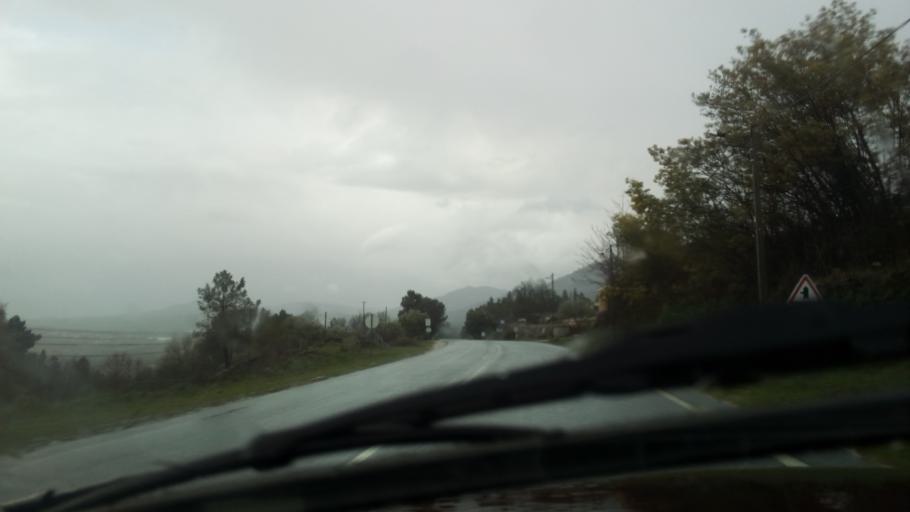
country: PT
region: Guarda
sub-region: Guarda
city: Guarda
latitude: 40.5773
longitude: -7.2956
